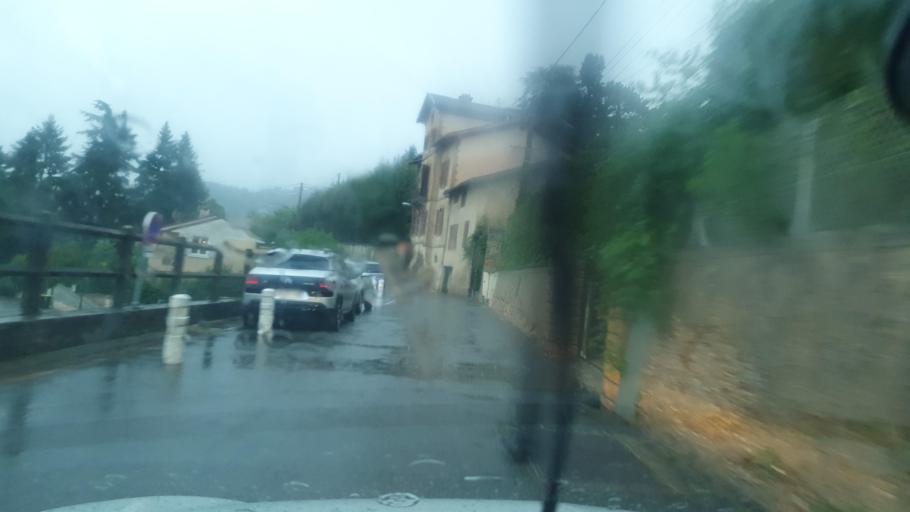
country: FR
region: Rhone-Alpes
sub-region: Departement du Rhone
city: Fontaines-sur-Saone
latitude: 45.8431
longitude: 4.8265
